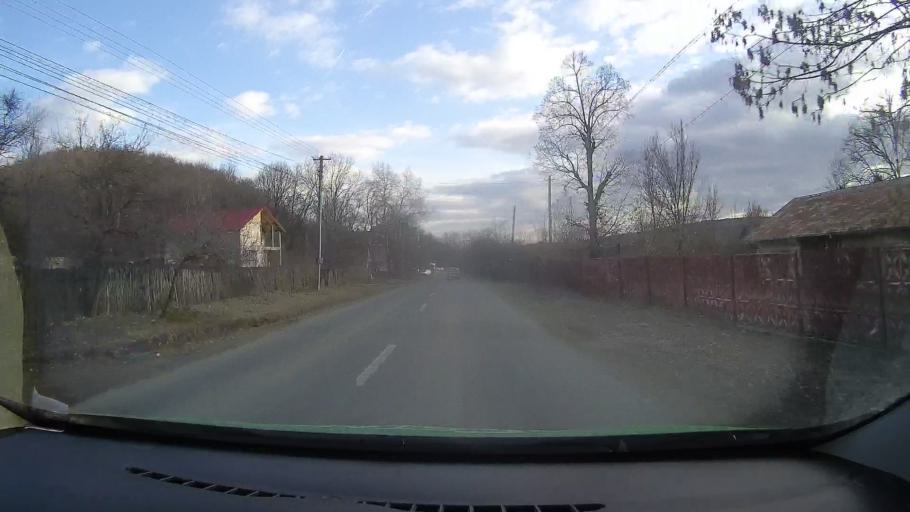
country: RO
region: Dambovita
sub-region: Comuna Ocnita
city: Ocnita
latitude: 44.9605
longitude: 25.5498
